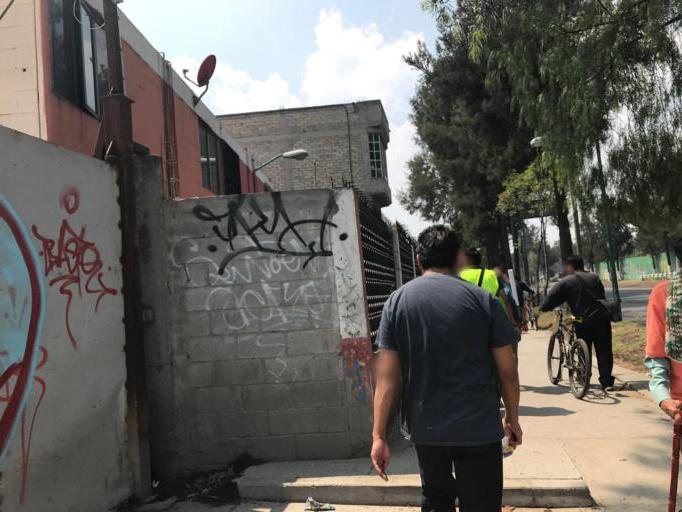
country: MX
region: Mexico City
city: Iztapalapa
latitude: 19.3144
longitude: -99.0782
